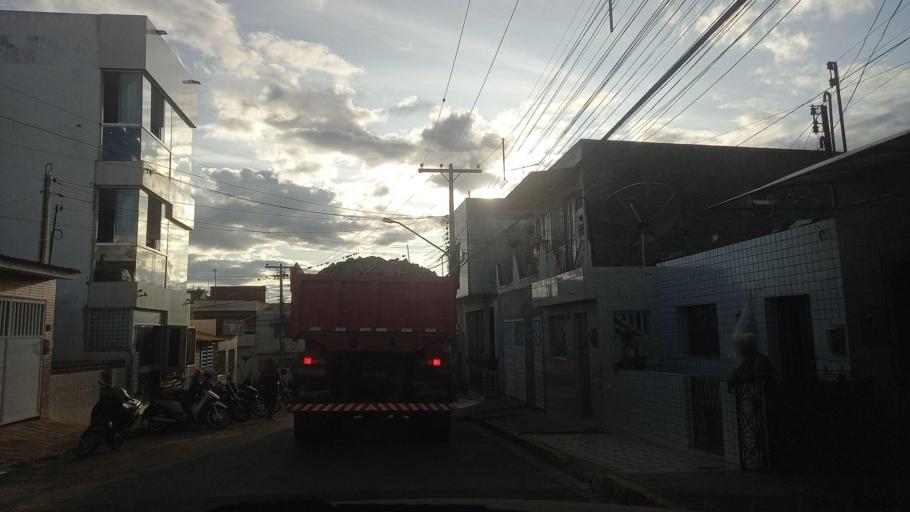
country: BR
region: Pernambuco
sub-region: Bezerros
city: Bezerros
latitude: -8.2380
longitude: -35.7568
